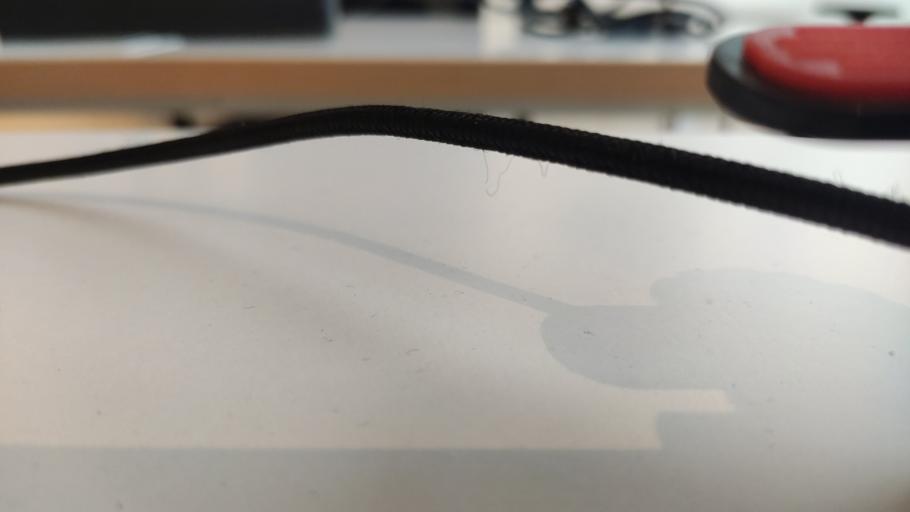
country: RU
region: Moskovskaya
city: Shevlyakovo
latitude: 56.3840
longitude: 36.8563
